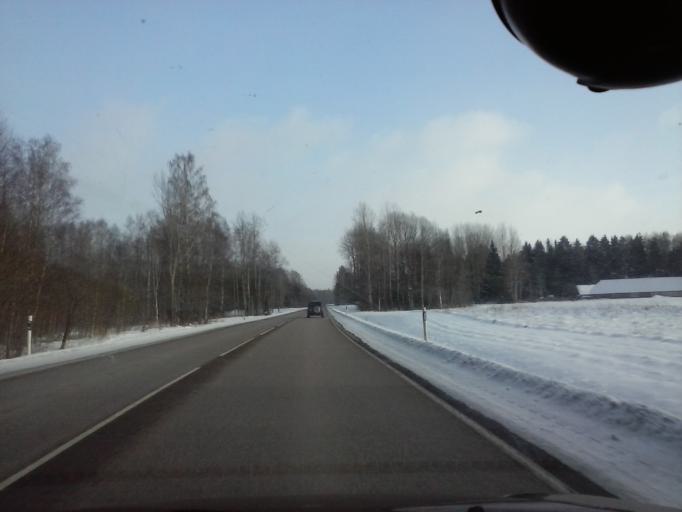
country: EE
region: Jogevamaa
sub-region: Poltsamaa linn
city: Poltsamaa
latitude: 58.4166
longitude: 26.0566
